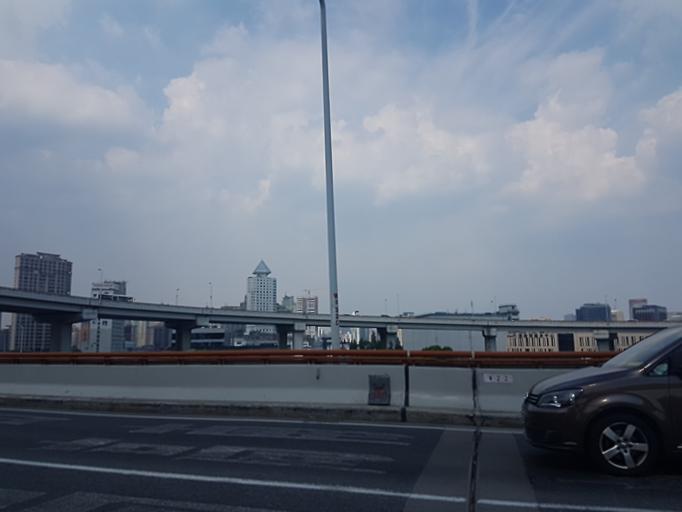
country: CN
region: Shanghai Shi
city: Luwan
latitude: 31.2099
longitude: 121.4966
